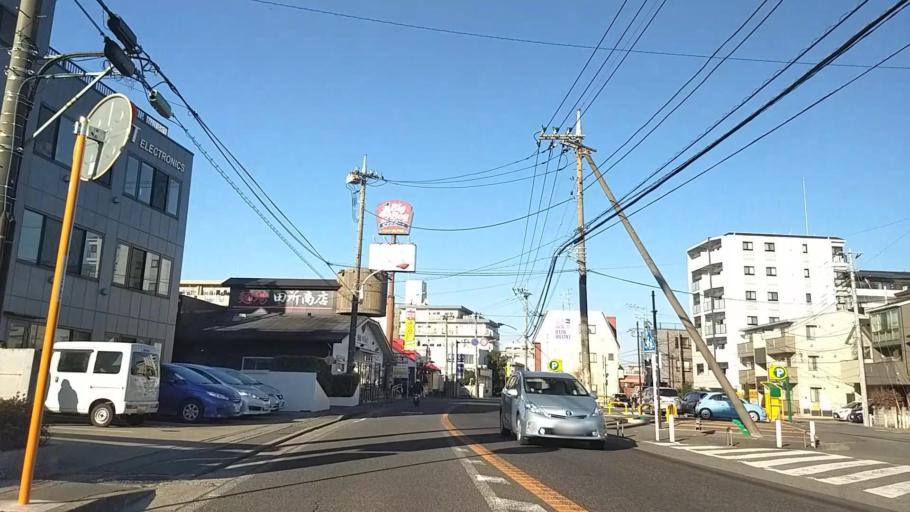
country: JP
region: Kanagawa
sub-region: Kawasaki-shi
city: Kawasaki
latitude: 35.5842
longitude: 139.6469
